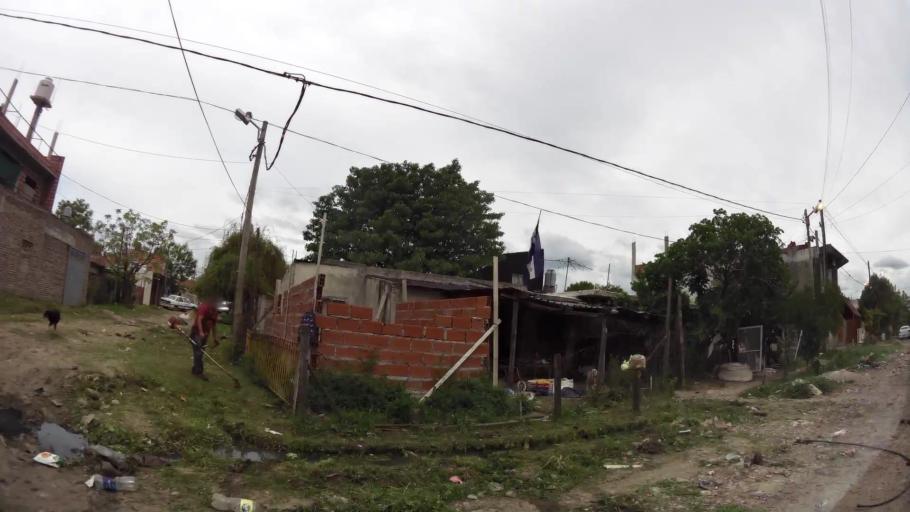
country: AR
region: Buenos Aires
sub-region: Partido de Quilmes
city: Quilmes
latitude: -34.7551
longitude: -58.2554
